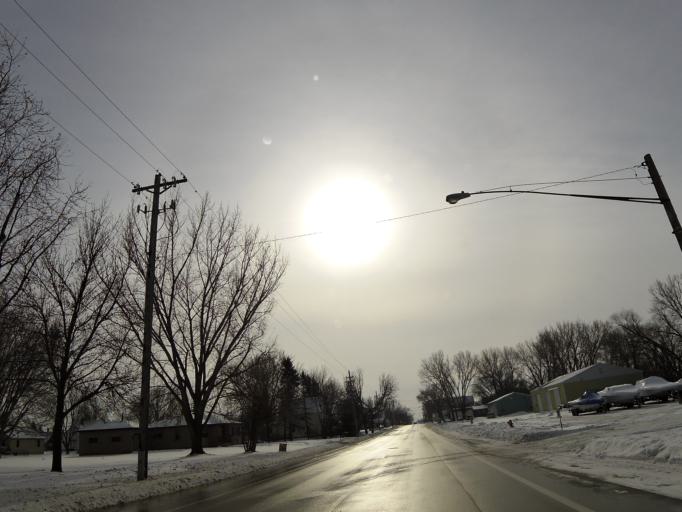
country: US
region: Minnesota
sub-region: McLeod County
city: Lester Prairie
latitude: 44.8867
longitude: -93.9703
